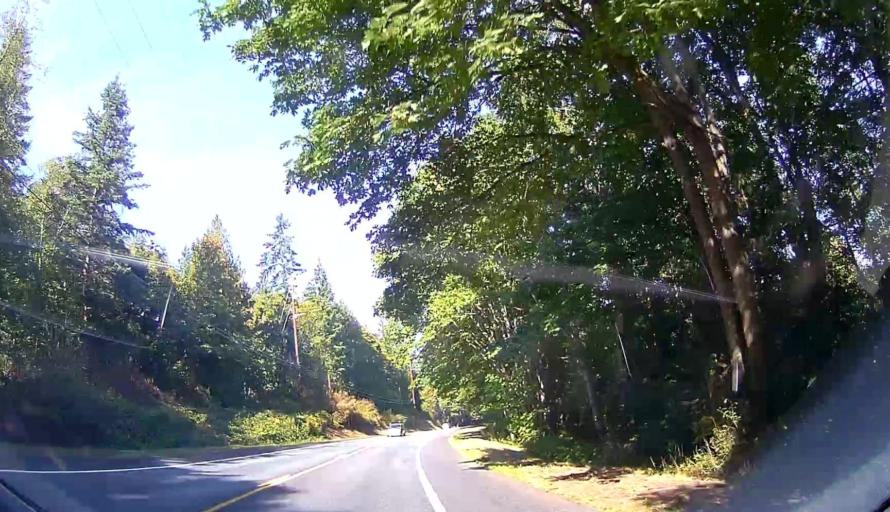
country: US
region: Washington
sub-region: Island County
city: Camano
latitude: 48.2013
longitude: -122.4841
